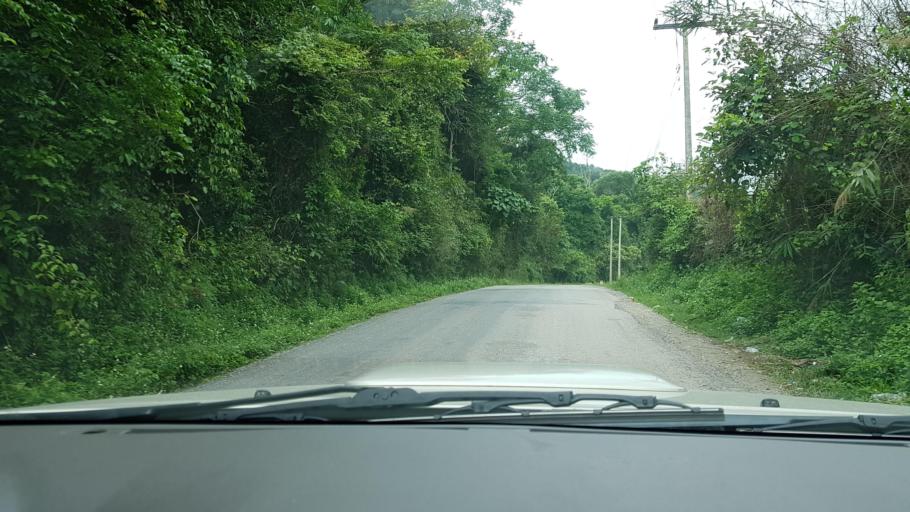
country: LA
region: Oudomxai
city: Muang Xay
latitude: 20.5497
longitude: 101.9086
